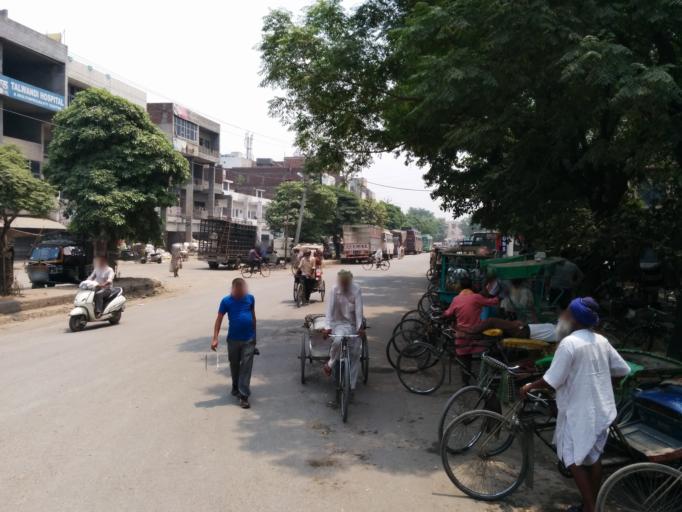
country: IN
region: Punjab
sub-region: Amritsar
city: Amritsar
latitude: 31.6287
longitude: 74.8856
